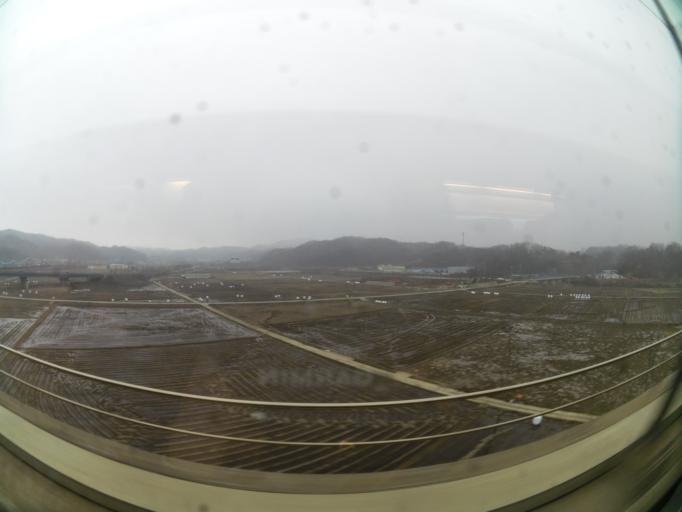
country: KR
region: Chungcheongnam-do
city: Cheonan
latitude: 36.7263
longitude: 127.1552
